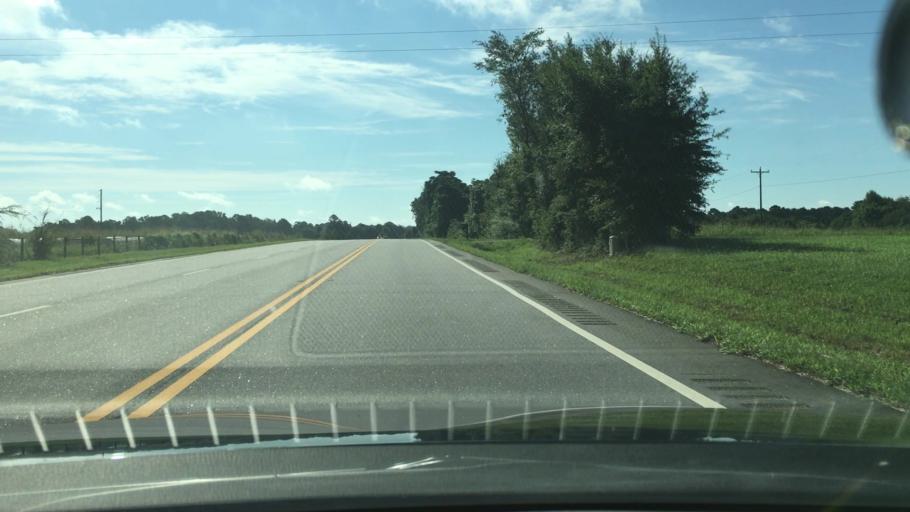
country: US
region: Georgia
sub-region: Putnam County
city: Jefferson
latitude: 33.4736
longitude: -83.4264
